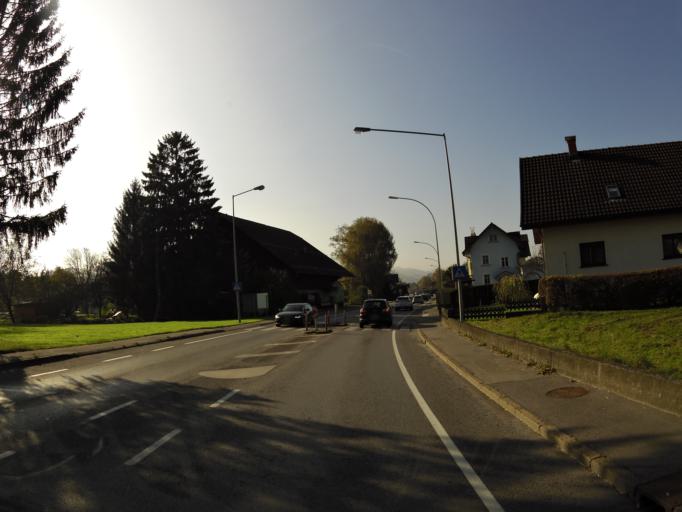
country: AT
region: Vorarlberg
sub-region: Politischer Bezirk Bregenz
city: Hochst
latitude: 47.4621
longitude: 9.6566
